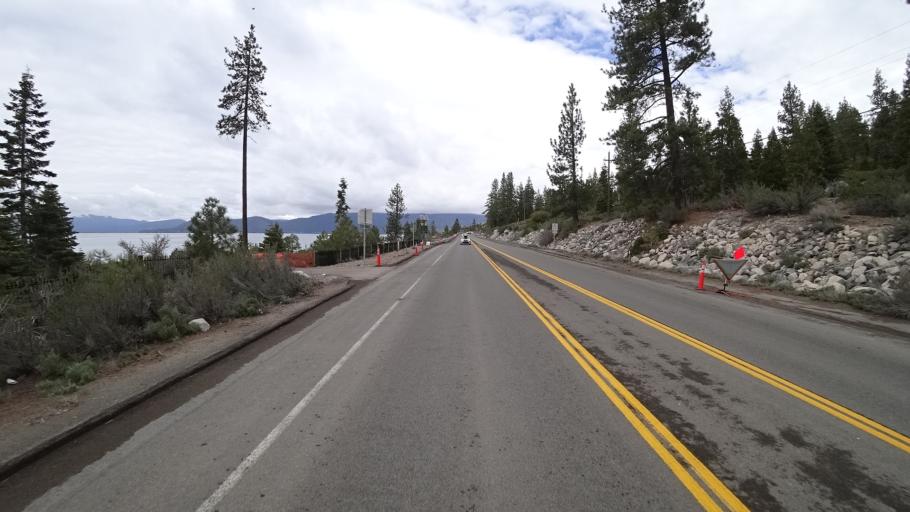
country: US
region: Nevada
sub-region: Washoe County
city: Incline Village
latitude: 39.2011
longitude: -119.9293
